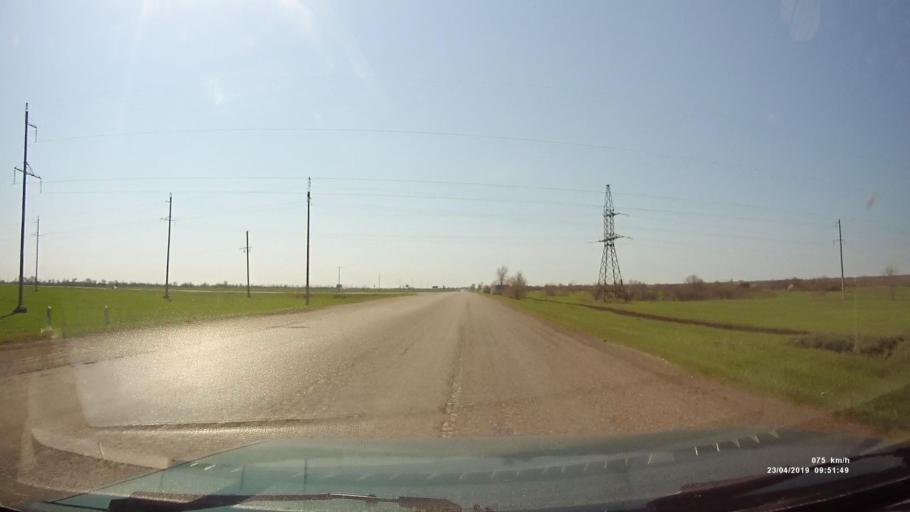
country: RU
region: Rostov
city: Orlovskiy
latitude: 46.8517
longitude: 42.0425
